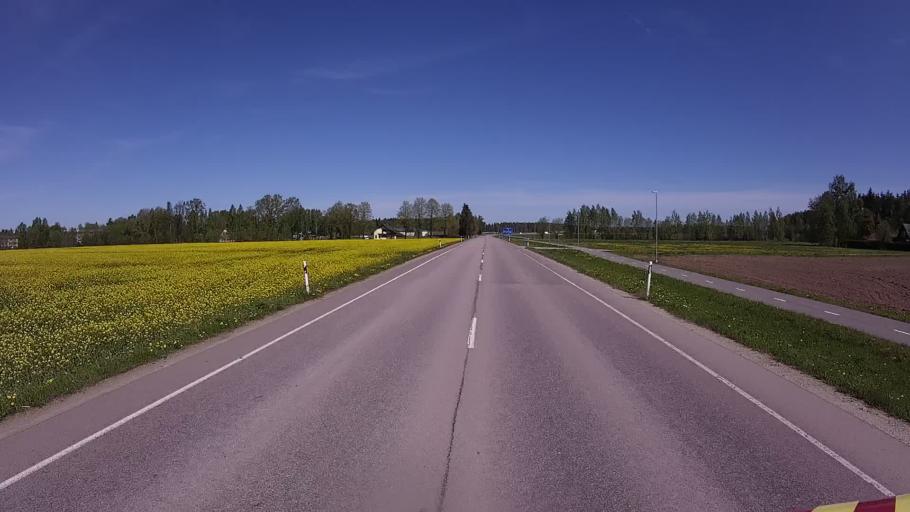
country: EE
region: Polvamaa
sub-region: Polva linn
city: Polva
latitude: 58.0834
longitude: 27.0905
